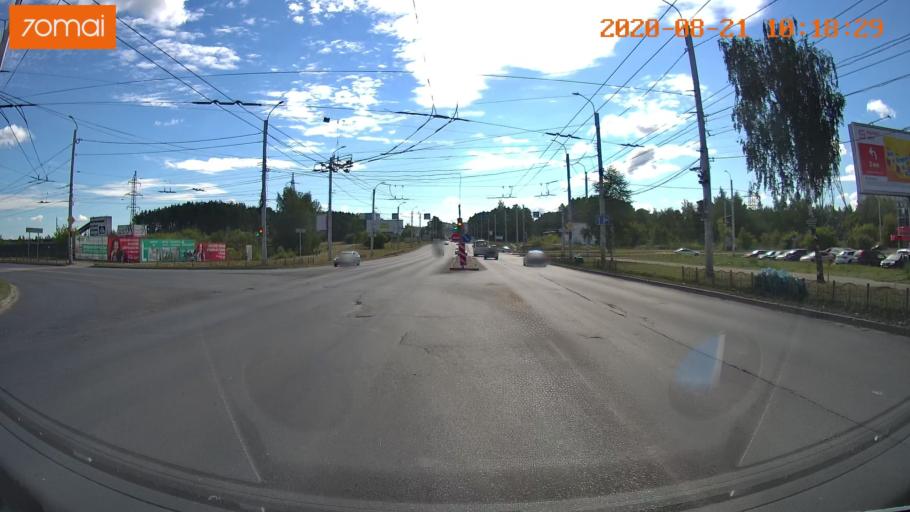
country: RU
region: Ivanovo
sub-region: Gorod Ivanovo
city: Ivanovo
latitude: 56.9609
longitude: 41.0283
